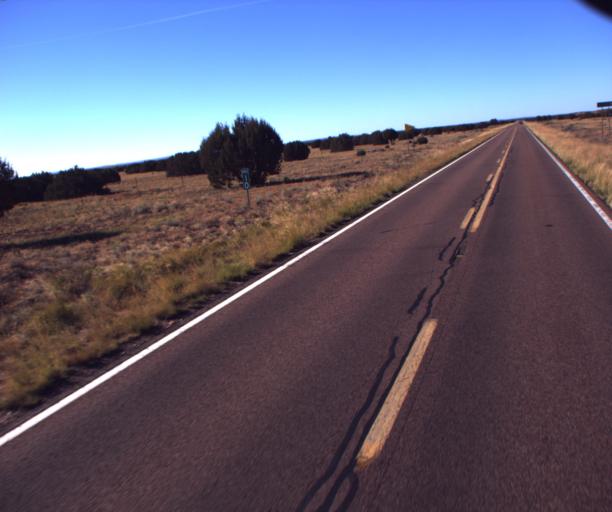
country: US
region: Arizona
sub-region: Navajo County
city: Heber-Overgaard
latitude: 34.5890
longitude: -110.3980
